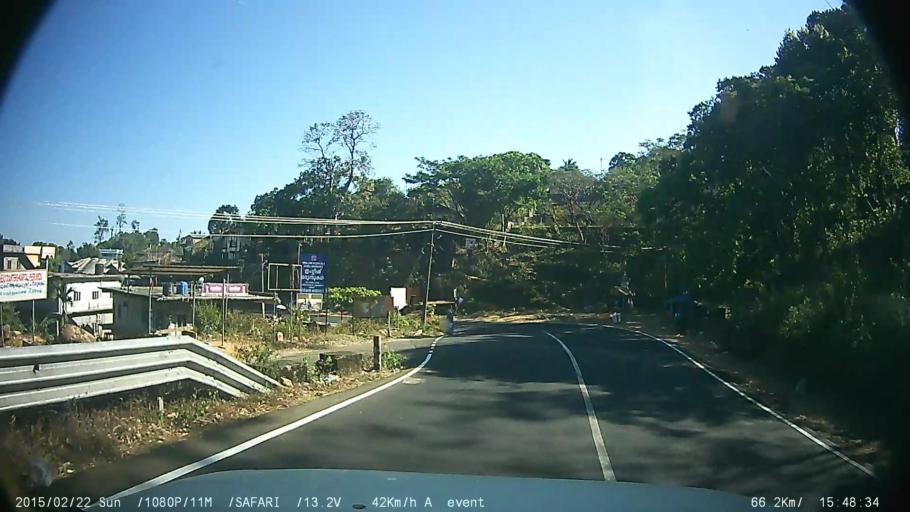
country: IN
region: Kerala
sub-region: Kottayam
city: Erattupetta
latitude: 9.5730
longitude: 76.9936
